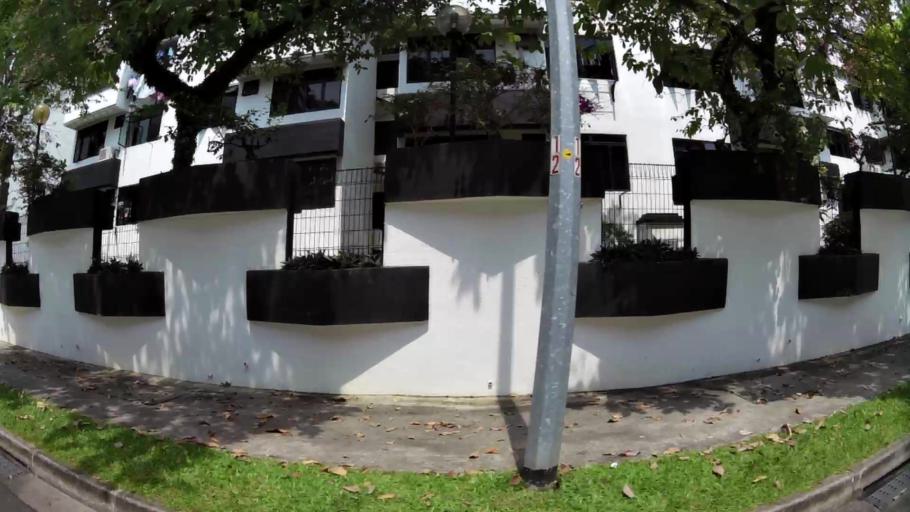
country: MY
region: Johor
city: Kampung Pasir Gudang Baru
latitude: 1.3776
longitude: 103.9582
